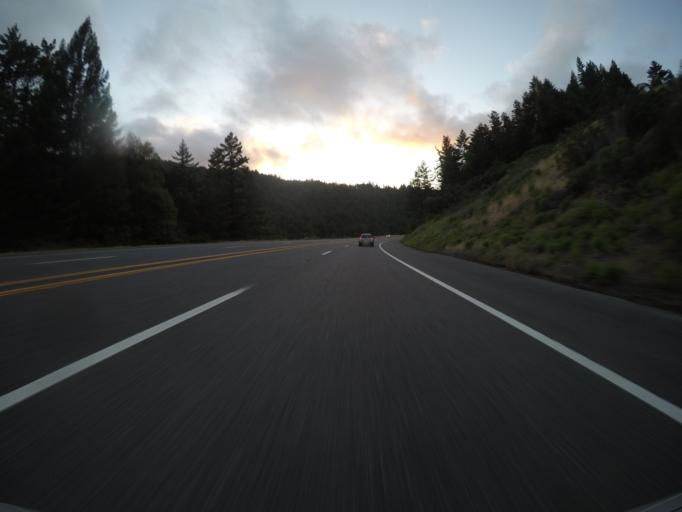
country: US
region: California
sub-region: Humboldt County
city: Redway
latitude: 40.0493
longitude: -123.7906
